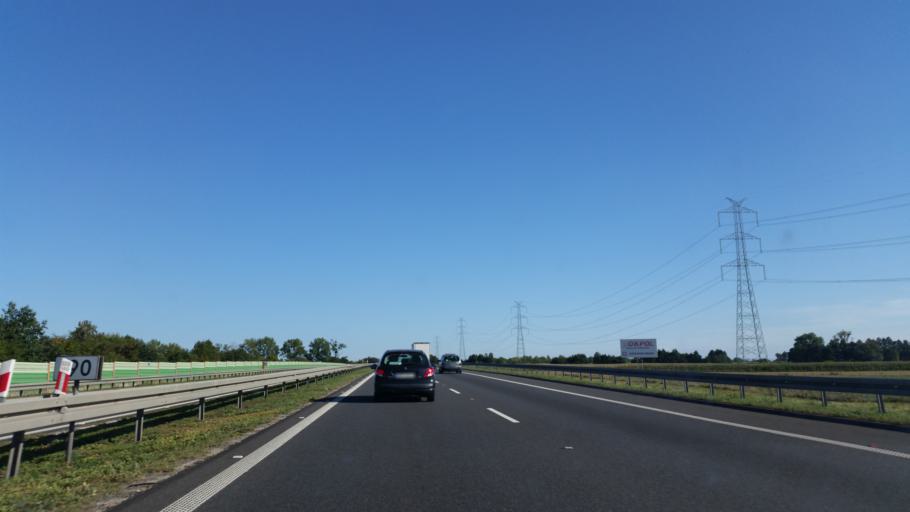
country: PL
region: Opole Voivodeship
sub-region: Powiat brzeski
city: Skarbimierz Osiedle
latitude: 50.8105
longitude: 17.3136
